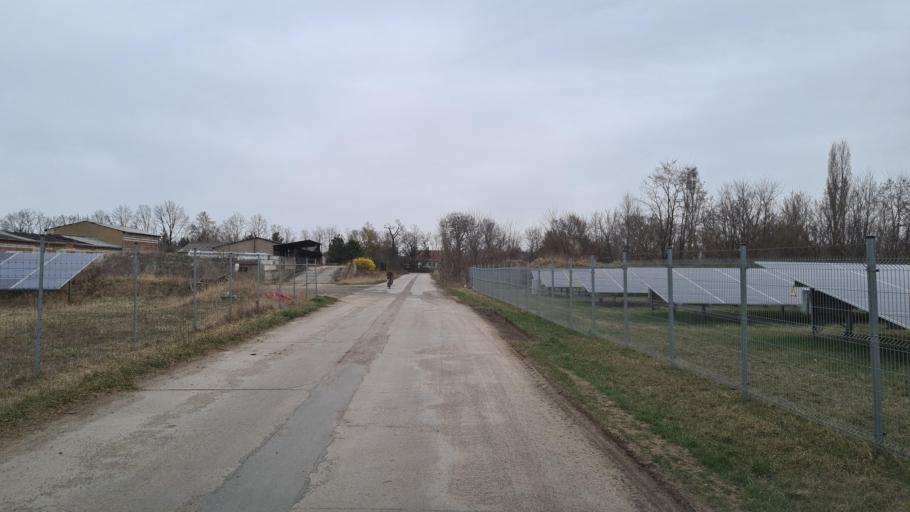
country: DE
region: Brandenburg
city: Elsterwerda
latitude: 51.4513
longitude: 13.5380
